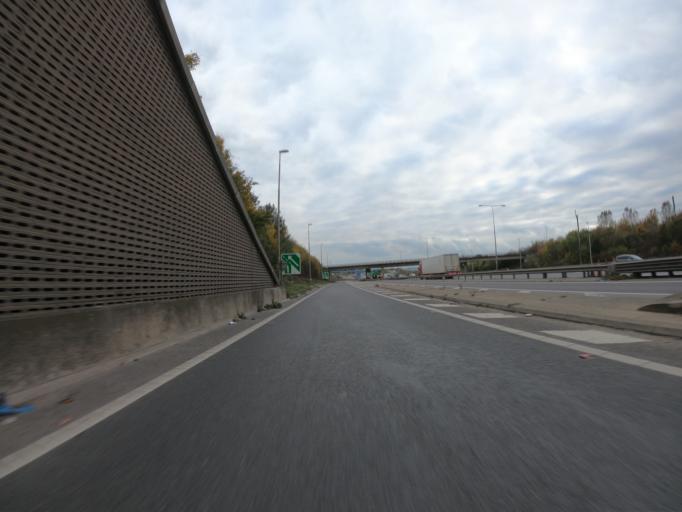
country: GB
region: England
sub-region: Kent
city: Dartford
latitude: 51.4350
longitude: 0.2394
